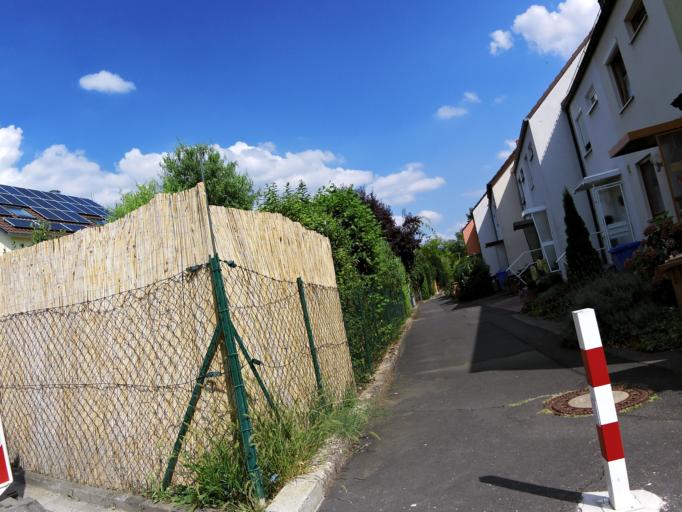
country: DE
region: Bavaria
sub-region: Regierungsbezirk Unterfranken
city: Estenfeld
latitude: 49.8248
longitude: 10.0055
